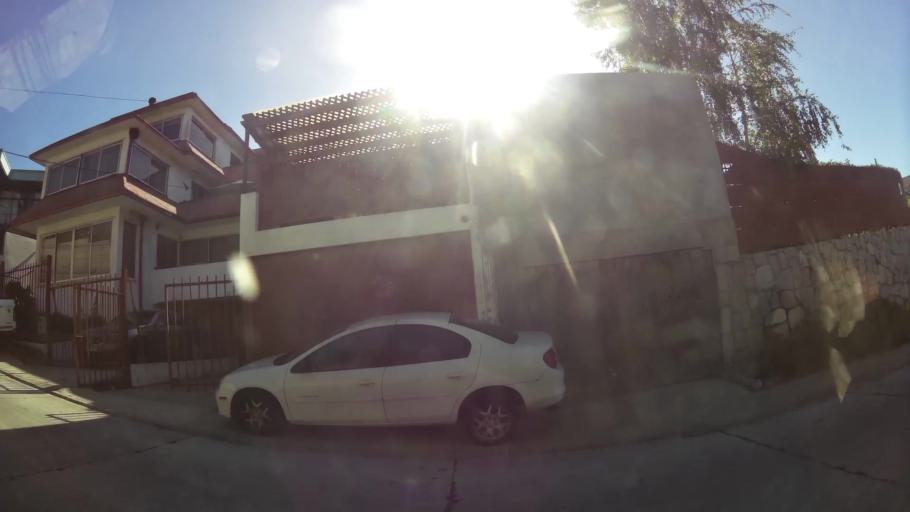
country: CL
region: Valparaiso
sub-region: Provincia de Valparaiso
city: Vina del Mar
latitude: -33.0368
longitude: -71.5566
